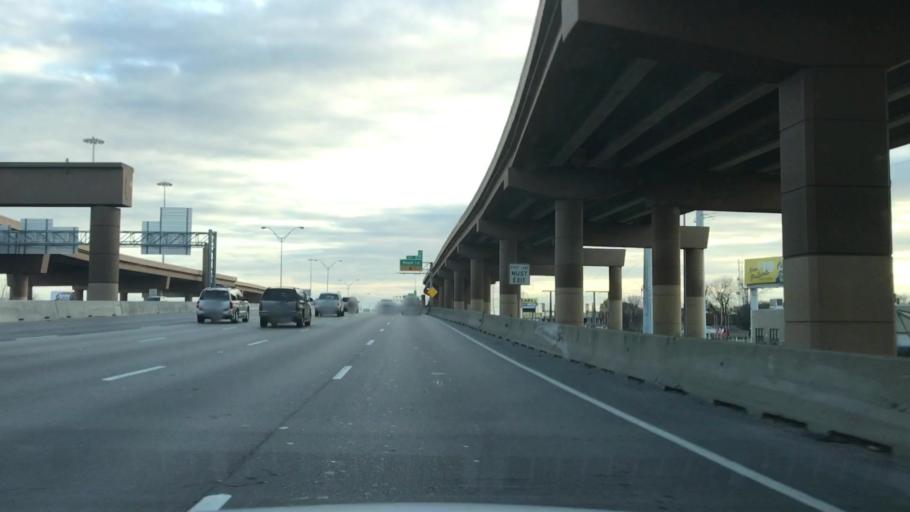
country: US
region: Texas
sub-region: Dallas County
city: Farmers Branch
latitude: 32.9020
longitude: -96.8982
